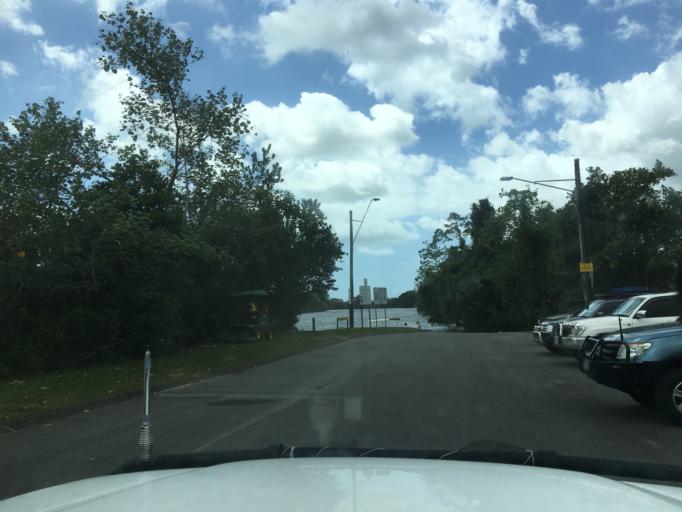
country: AU
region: Queensland
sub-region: Cairns
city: Woree
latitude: -17.2170
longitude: 145.9203
